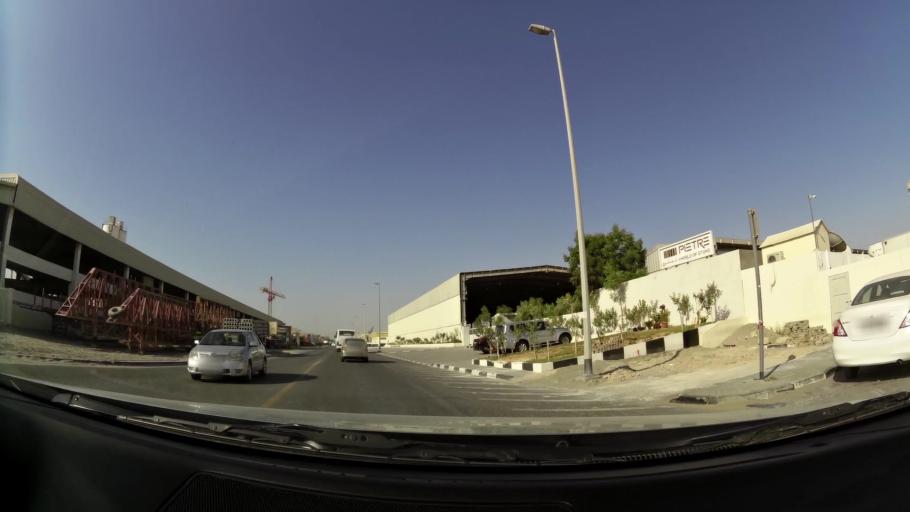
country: AE
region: Dubai
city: Dubai
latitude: 25.1196
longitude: 55.2185
